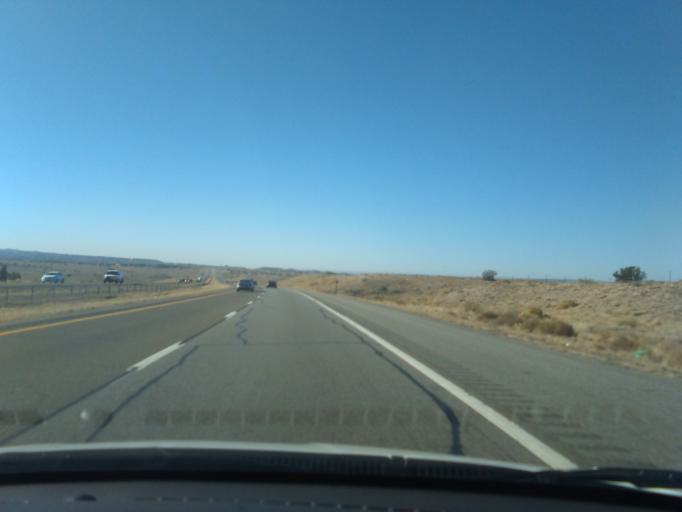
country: US
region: New Mexico
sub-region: Sandoval County
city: Santo Domingo Pueblo
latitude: 35.4463
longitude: -106.3627
